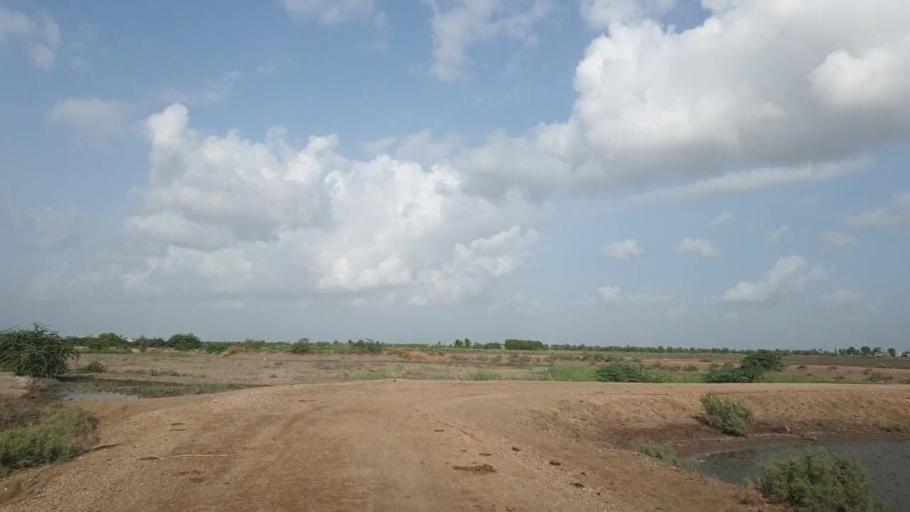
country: PK
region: Sindh
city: Kadhan
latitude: 24.6305
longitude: 69.0859
